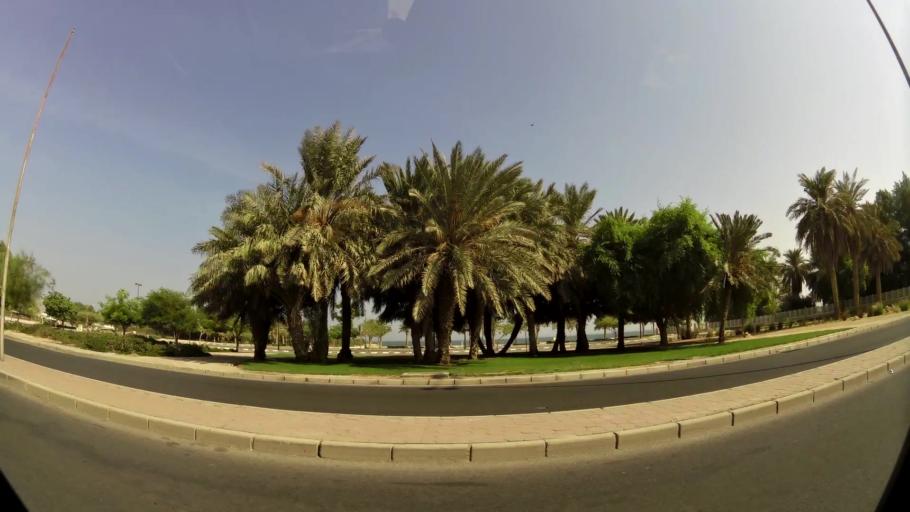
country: KW
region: Al Ahmadi
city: Al Manqaf
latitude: 29.0900
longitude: 48.1378
